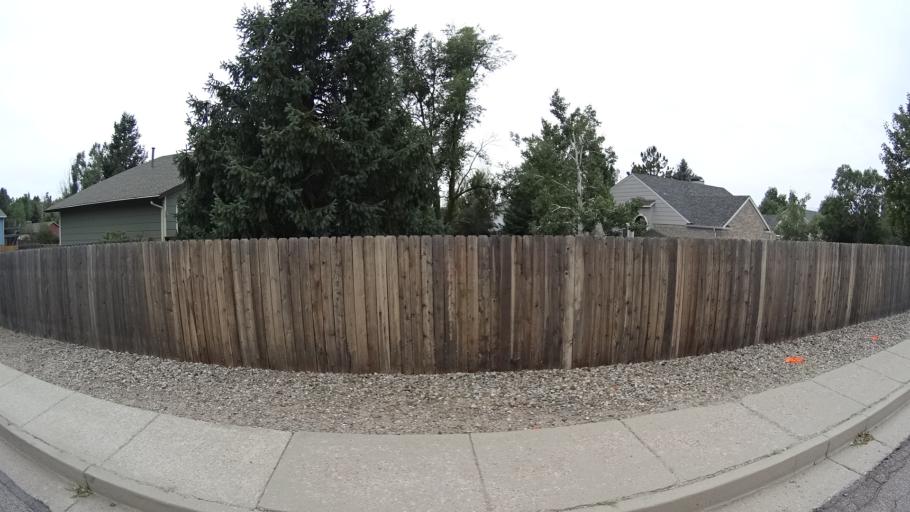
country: US
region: Colorado
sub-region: El Paso County
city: Cimarron Hills
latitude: 38.9069
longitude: -104.7272
